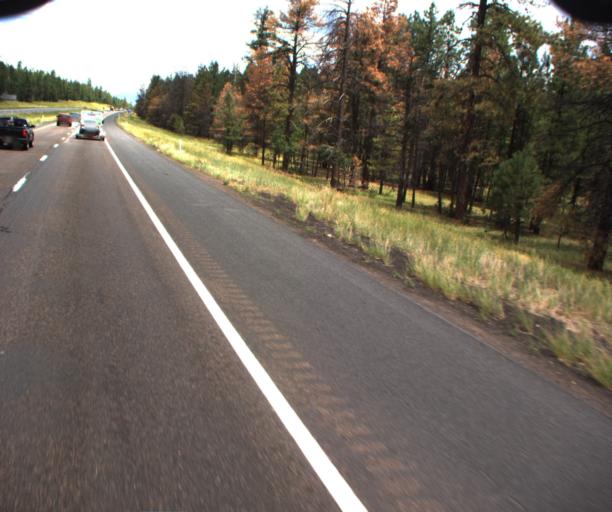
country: US
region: Arizona
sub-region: Coconino County
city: Mountainaire
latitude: 34.9898
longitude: -111.6868
